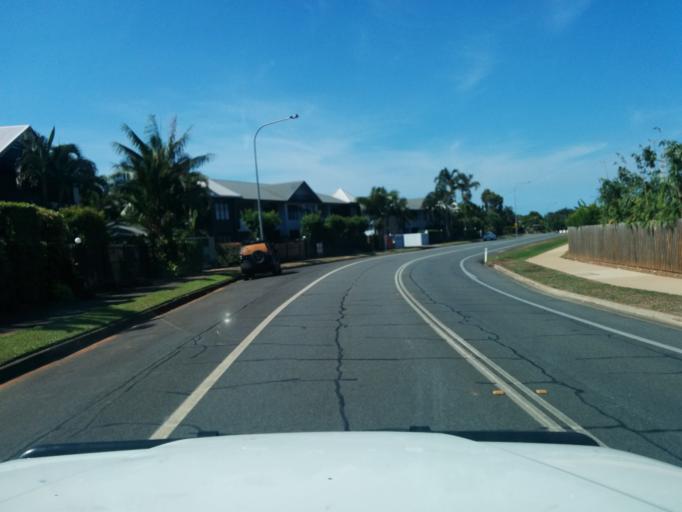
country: AU
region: Queensland
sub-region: Cairns
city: Redlynch
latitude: -16.8931
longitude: 145.6947
